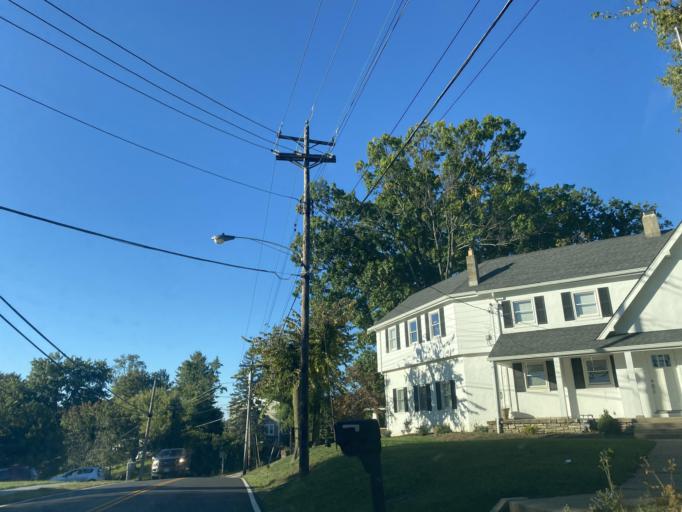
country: US
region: Kentucky
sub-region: Campbell County
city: Dayton
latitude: 39.1073
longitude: -84.4585
